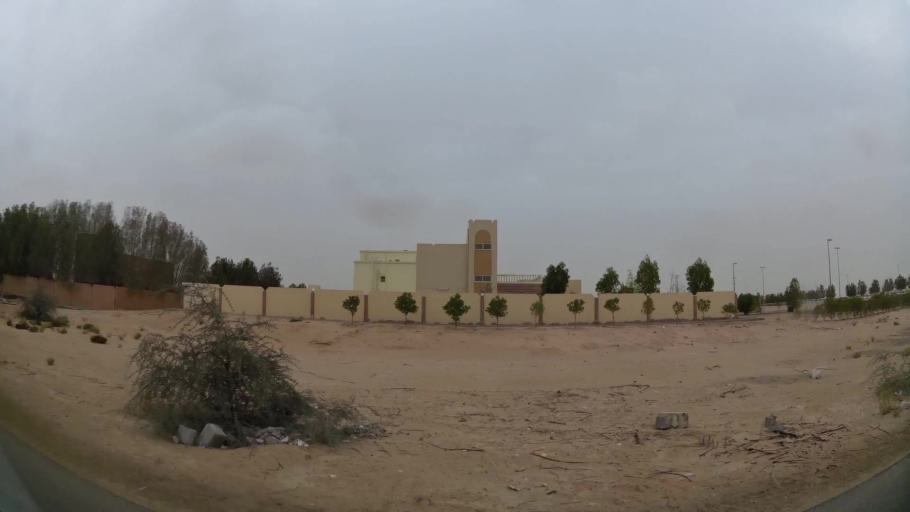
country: AE
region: Abu Dhabi
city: Abu Dhabi
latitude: 24.3773
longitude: 54.7071
